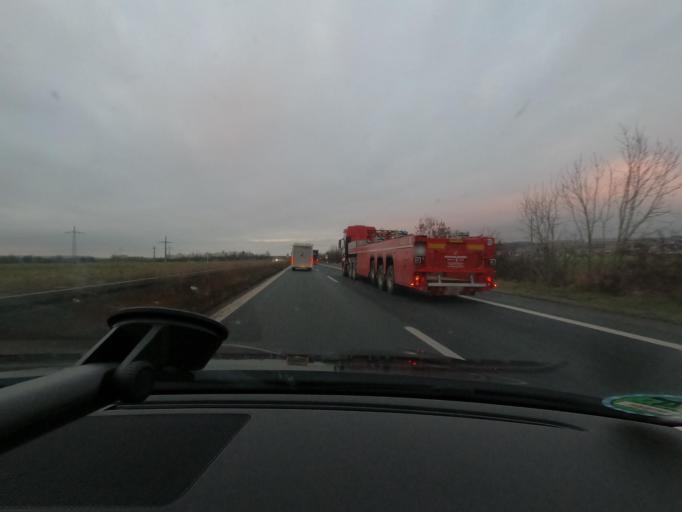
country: DE
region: Bavaria
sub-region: Upper Franconia
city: Eggolsheim
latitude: 49.7808
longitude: 11.0407
